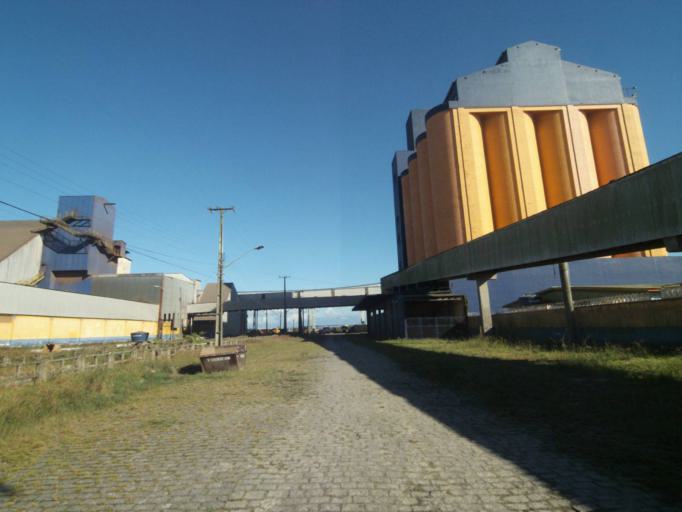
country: BR
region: Parana
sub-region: Paranagua
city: Paranagua
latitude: -25.5032
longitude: -48.5242
